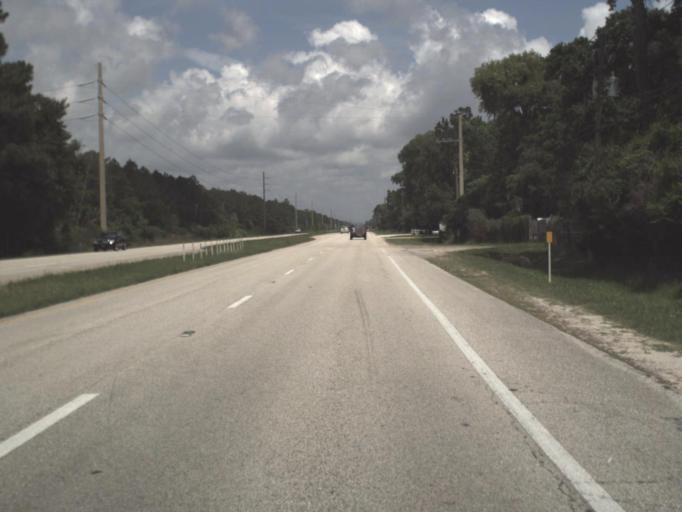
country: US
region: Florida
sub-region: Saint Johns County
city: Villano Beach
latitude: 29.9743
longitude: -81.3576
